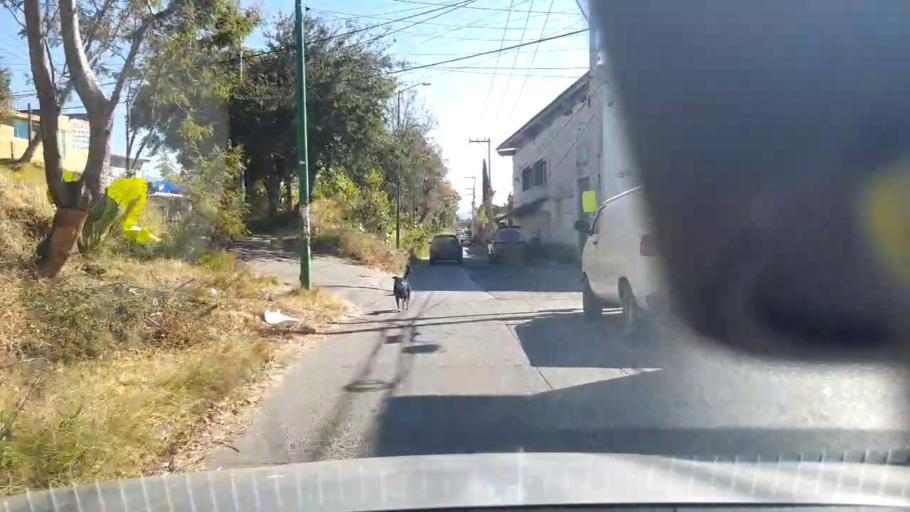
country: MX
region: Morelos
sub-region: Cuernavaca
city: Colonia los Cerritos
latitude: 18.9639
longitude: -99.2247
